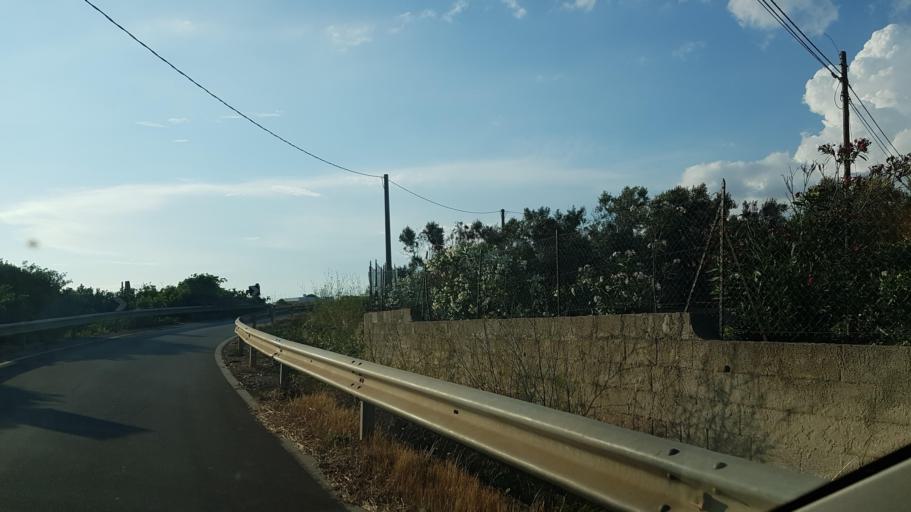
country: IT
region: Apulia
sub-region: Provincia di Lecce
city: Gemini
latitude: 39.8466
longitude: 18.2078
